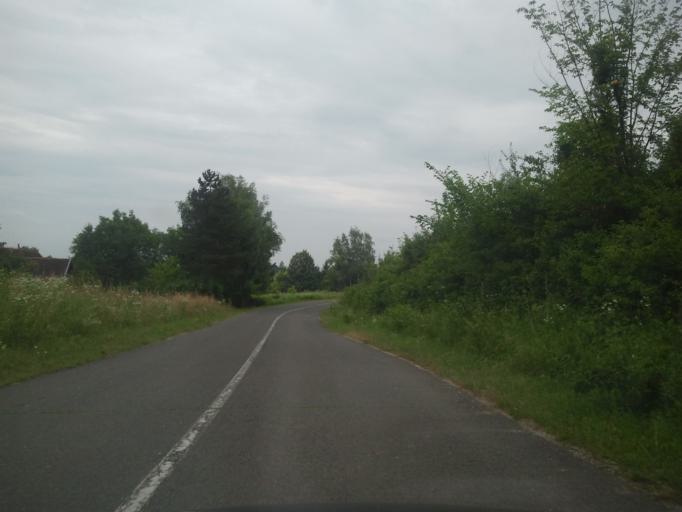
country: HR
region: Sisacko-Moslavacka
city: Gvozd
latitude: 45.4111
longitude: 15.9374
